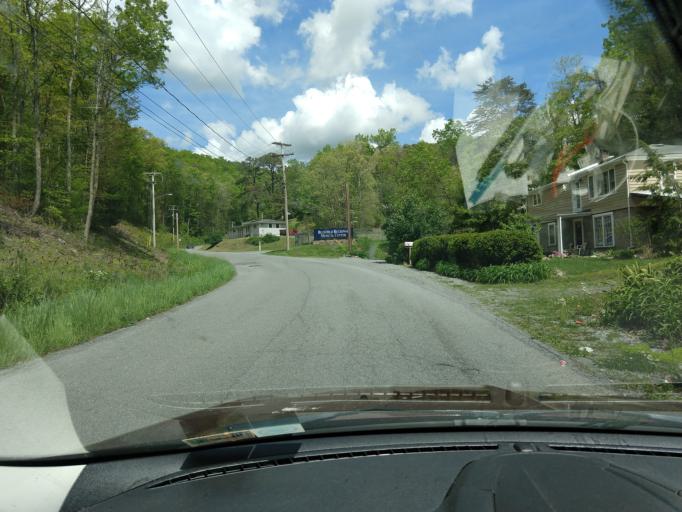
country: US
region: West Virginia
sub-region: Mercer County
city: Bluefield
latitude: 37.2529
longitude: -81.2392
